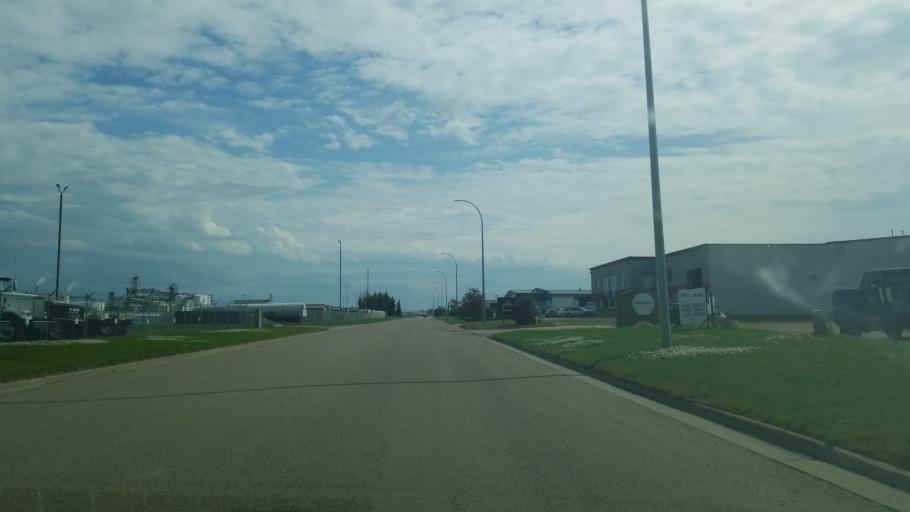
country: CA
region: Saskatchewan
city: Lloydminster
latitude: 53.2906
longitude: -110.0368
